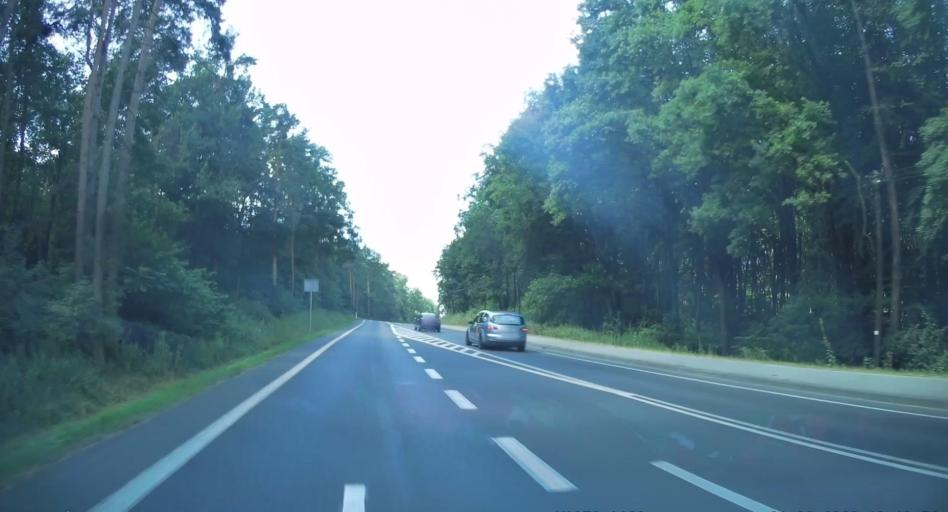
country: PL
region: Subcarpathian Voivodeship
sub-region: Powiat debicki
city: Brzeznica
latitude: 50.0985
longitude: 21.4756
